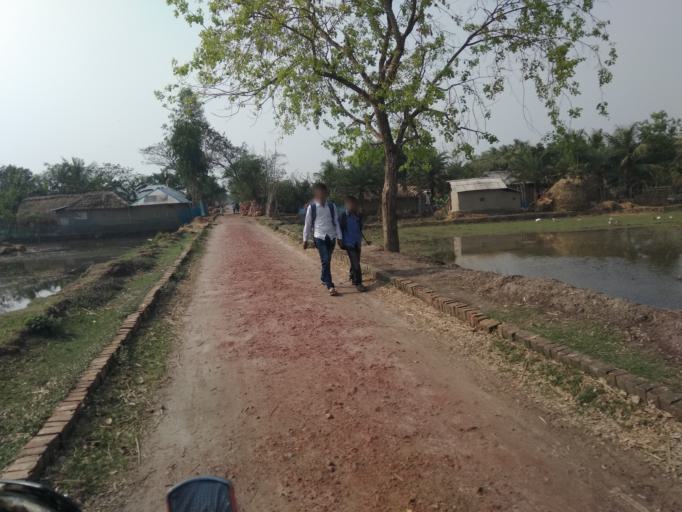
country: IN
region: West Bengal
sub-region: North 24 Parganas
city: Gosaba
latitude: 22.2625
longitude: 89.1154
